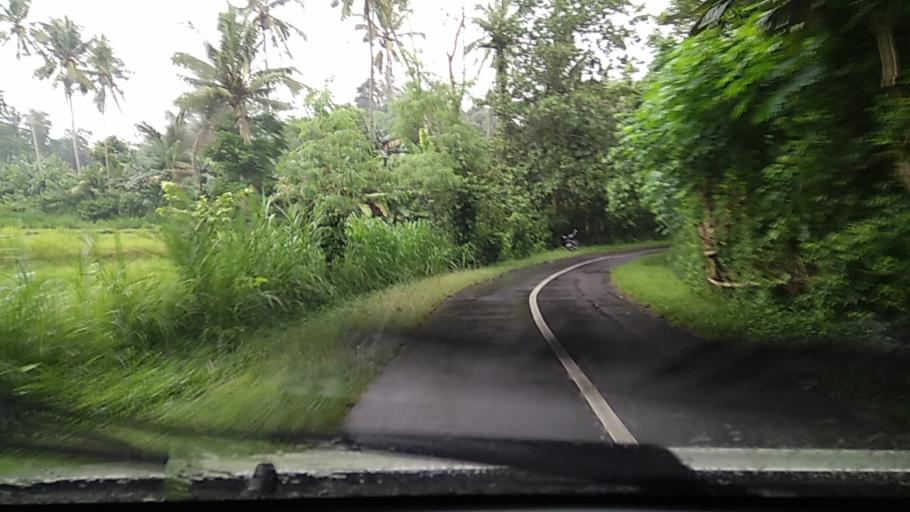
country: ID
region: Bali
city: Tiyingtali Kelod
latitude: -8.4142
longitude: 115.6187
